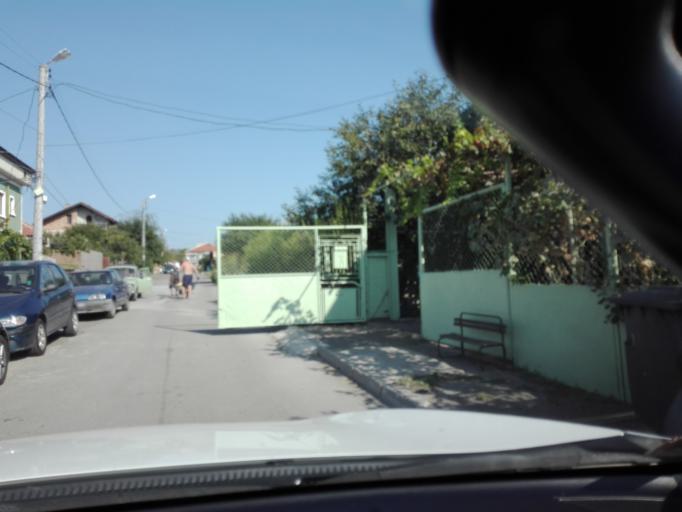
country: BG
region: Burgas
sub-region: Obshtina Kameno
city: Kameno
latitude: 42.6236
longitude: 27.3931
